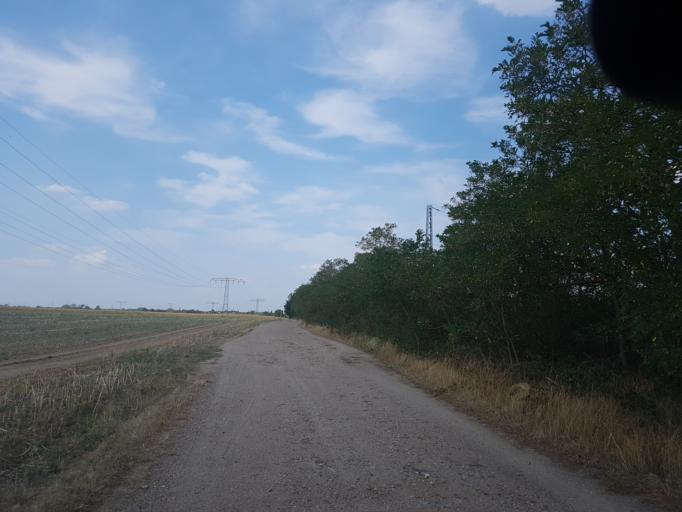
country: DE
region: Saxony
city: Wulknitz
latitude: 51.3595
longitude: 13.3780
